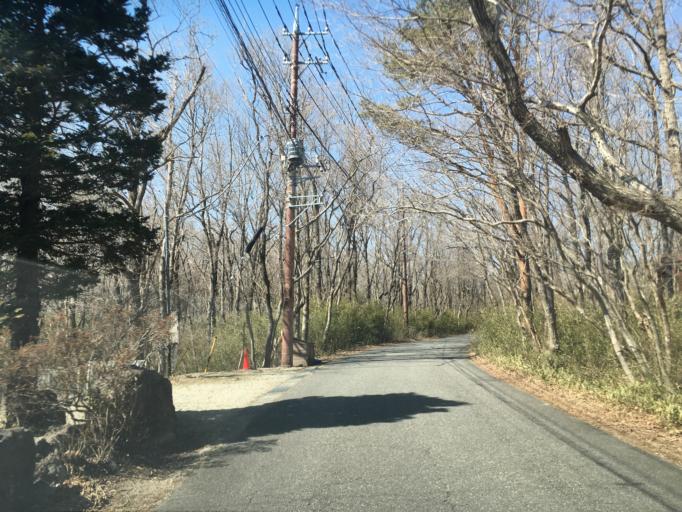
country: JP
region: Tochigi
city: Kuroiso
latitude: 37.0715
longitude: 140.0033
